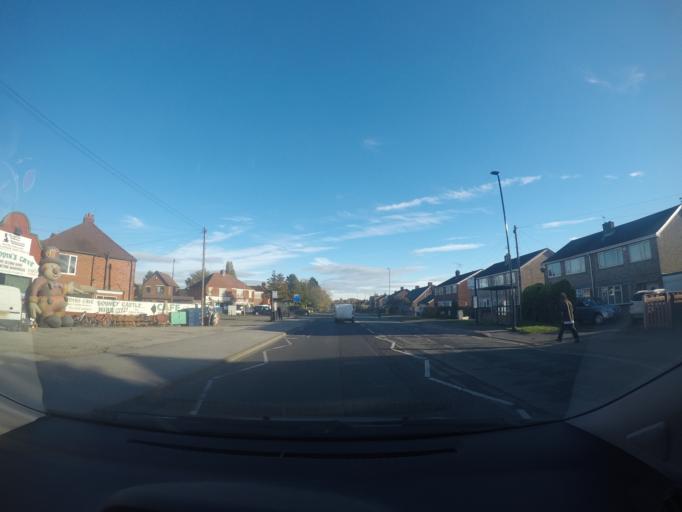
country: GB
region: England
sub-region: City of York
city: Nether Poppleton
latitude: 53.9666
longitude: -1.1268
